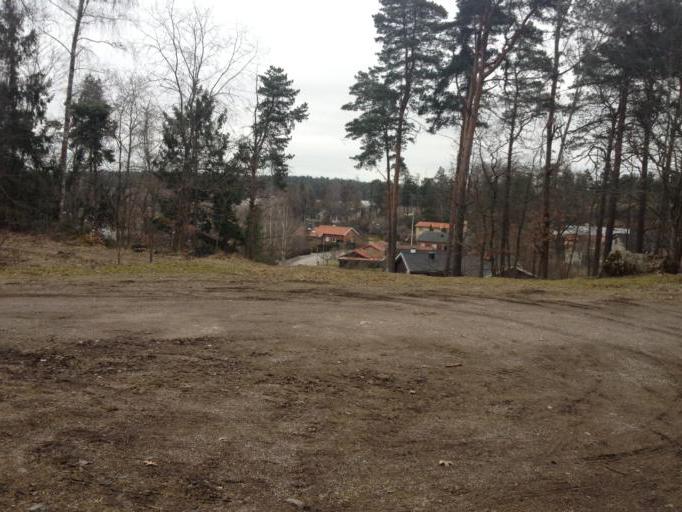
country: SE
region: Vaestmanland
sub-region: Kopings Kommun
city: Koping
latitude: 59.5125
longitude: 16.0088
